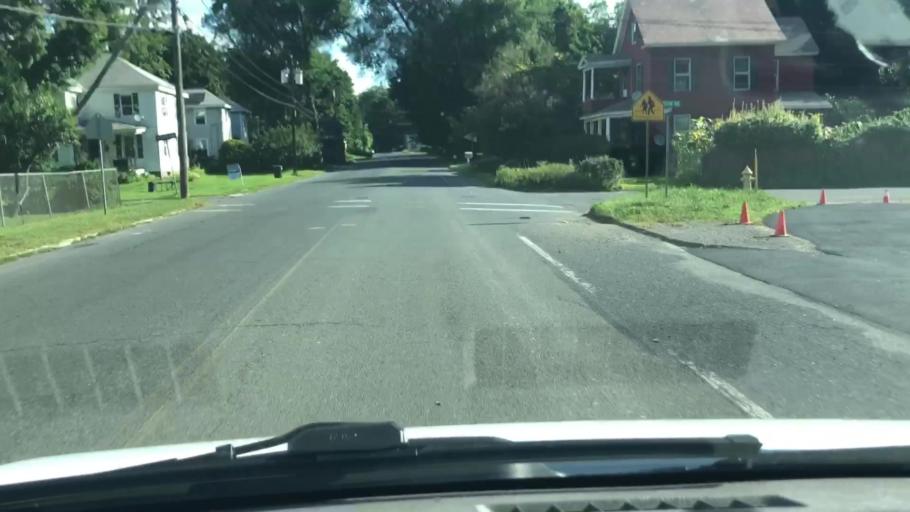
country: US
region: Massachusetts
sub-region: Franklin County
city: Greenfield
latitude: 42.5743
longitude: -72.5821
